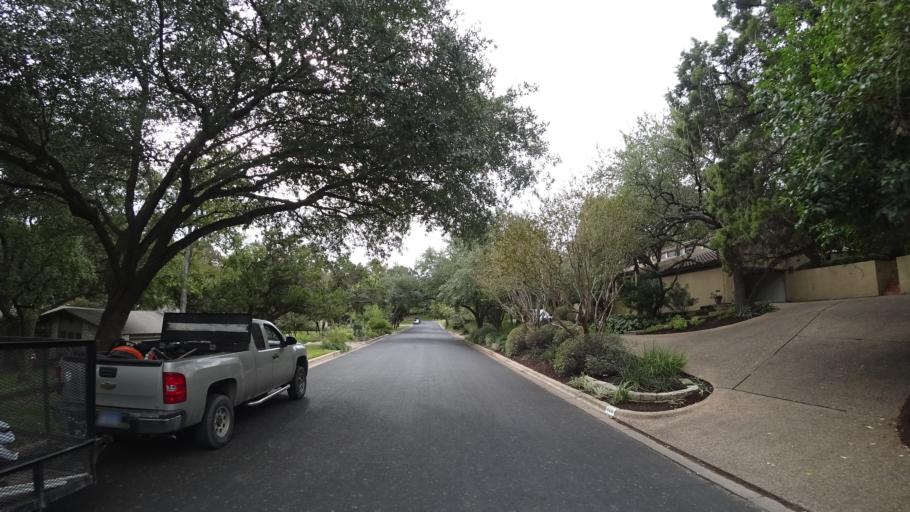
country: US
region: Texas
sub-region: Travis County
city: West Lake Hills
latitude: 30.3022
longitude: -97.7702
